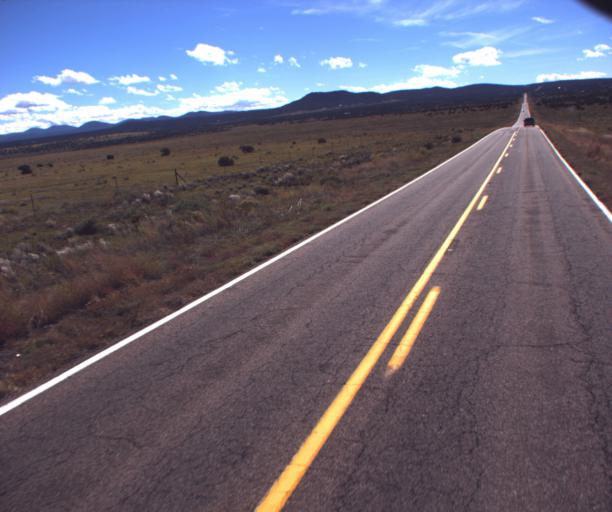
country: US
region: Arizona
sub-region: Navajo County
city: White Mountain Lake
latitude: 34.3564
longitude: -109.7128
